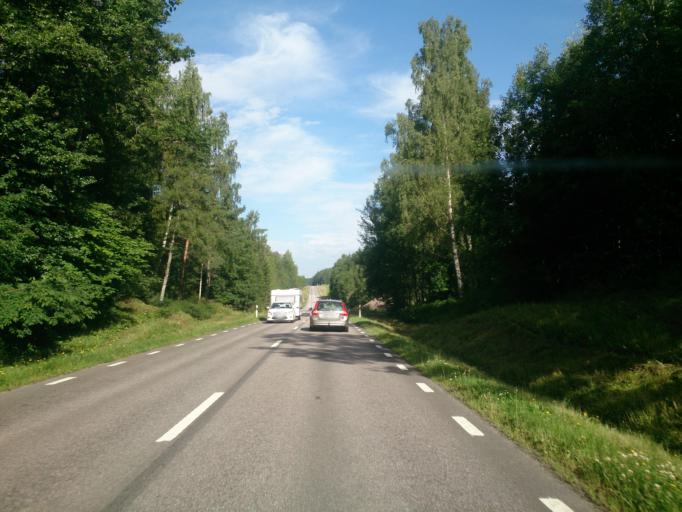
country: SE
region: OEstergoetland
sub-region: Atvidabergs Kommun
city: Atvidaberg
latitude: 58.2730
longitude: 15.9183
